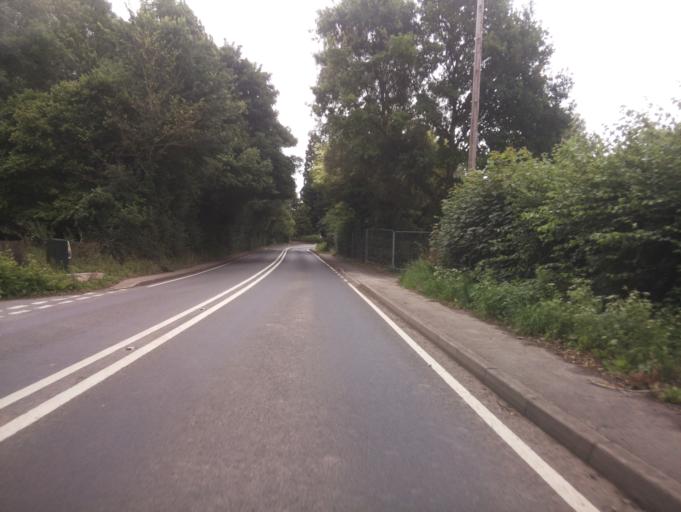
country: GB
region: England
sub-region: Worcestershire
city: Upton upon Severn
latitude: 52.0938
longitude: -2.2087
